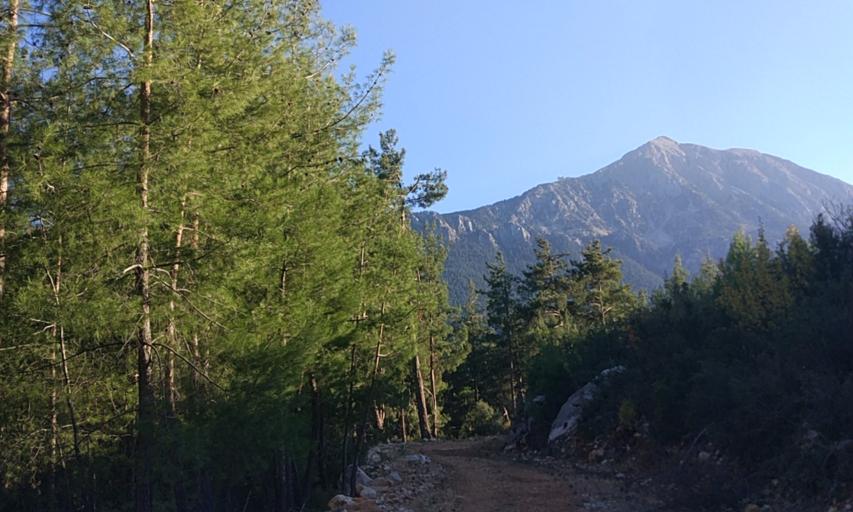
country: TR
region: Antalya
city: Altinyaka
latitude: 36.5921
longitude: 30.4266
